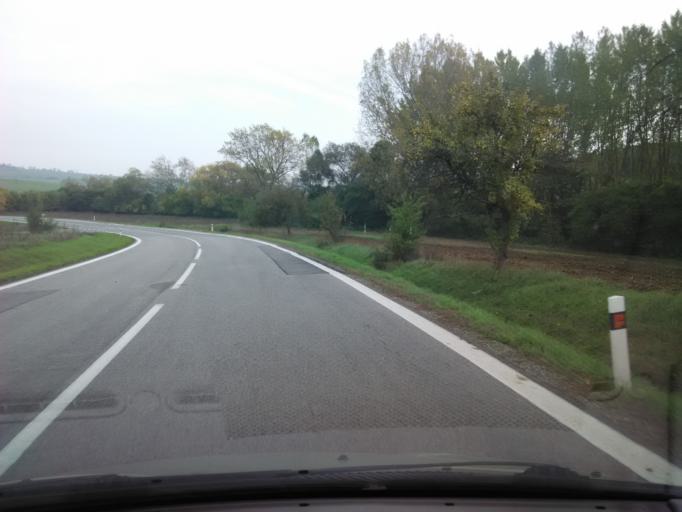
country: SK
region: Nitriansky
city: Svodin
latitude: 48.0323
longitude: 18.4500
